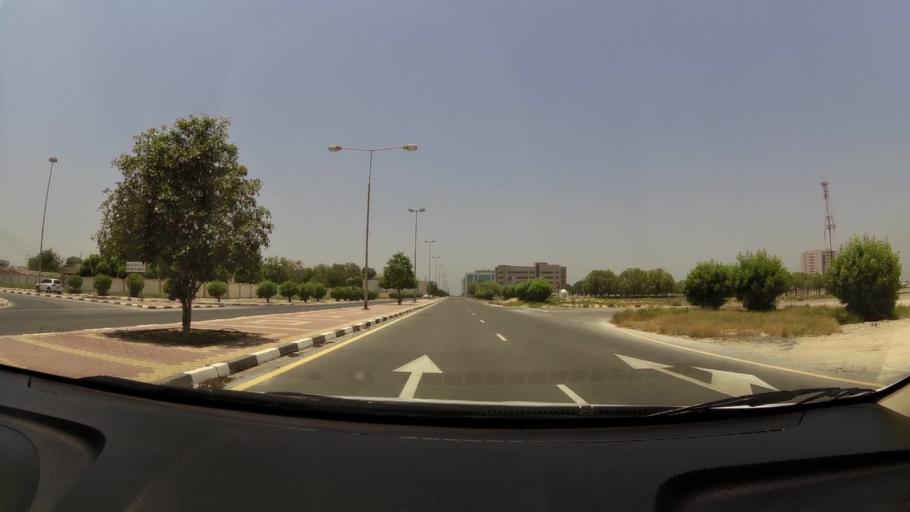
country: AE
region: Umm al Qaywayn
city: Umm al Qaywayn
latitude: 25.5741
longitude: 55.5627
